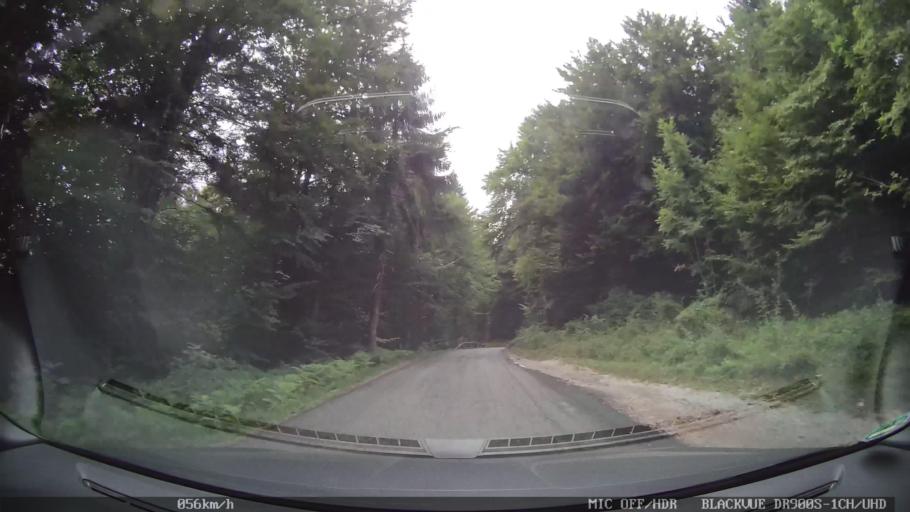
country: HR
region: Licko-Senjska
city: Jezerce
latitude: 44.9265
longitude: 15.5690
